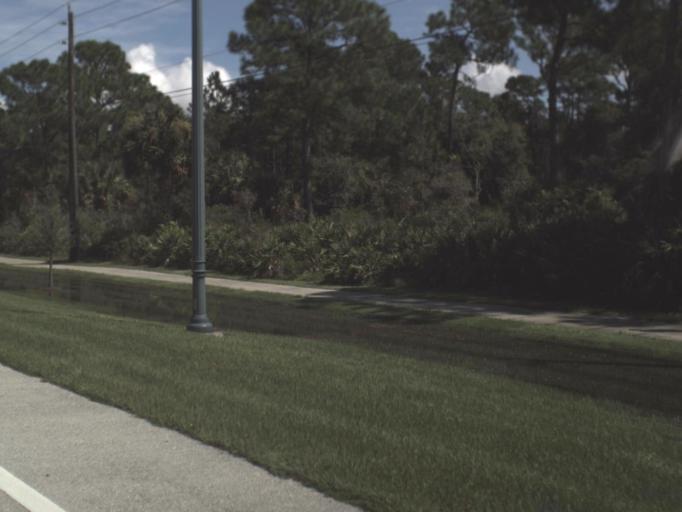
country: US
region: Florida
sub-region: Sarasota County
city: North Port
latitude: 27.0606
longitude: -82.1570
